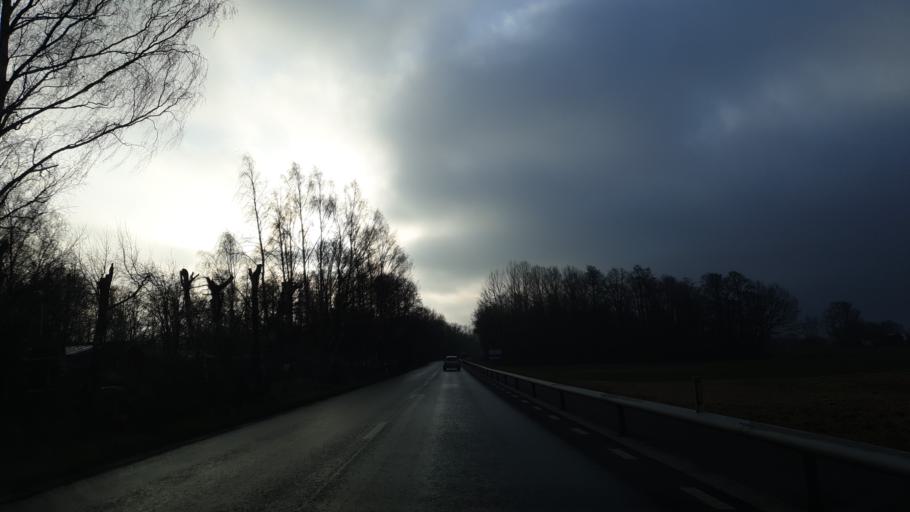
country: SE
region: Blekinge
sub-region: Karlshamns Kommun
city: Morrum
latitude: 56.1342
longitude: 14.6722
